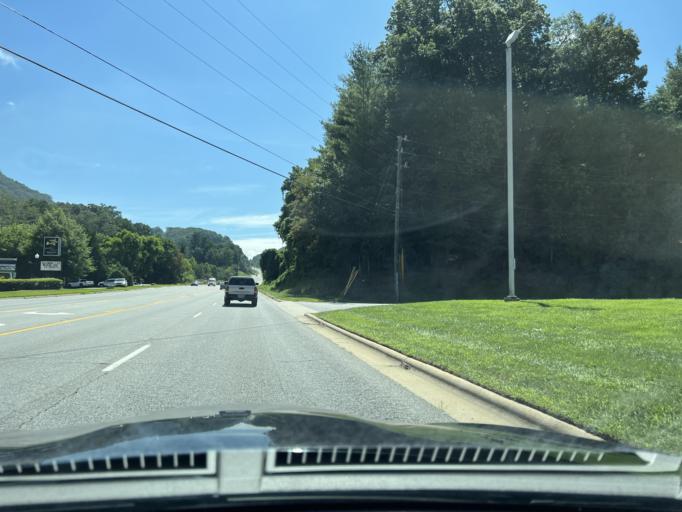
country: US
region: North Carolina
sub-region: Buncombe County
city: Biltmore Forest
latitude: 35.5510
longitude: -82.4725
